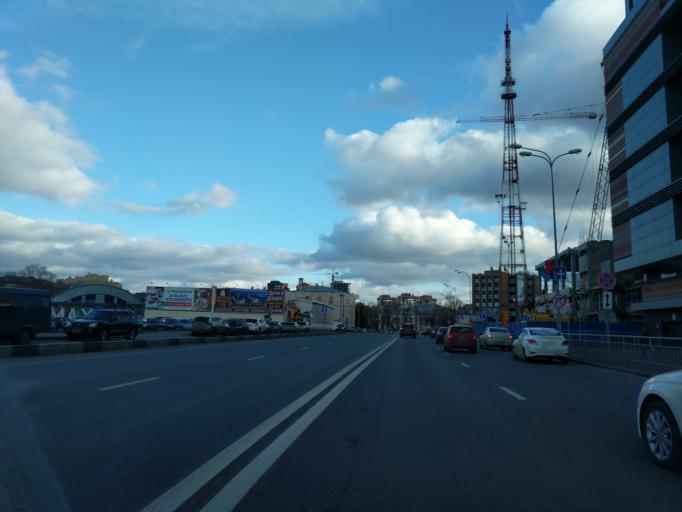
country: RU
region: Nizjnij Novgorod
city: Nizhniy Novgorod
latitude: 56.3096
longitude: 43.9881
